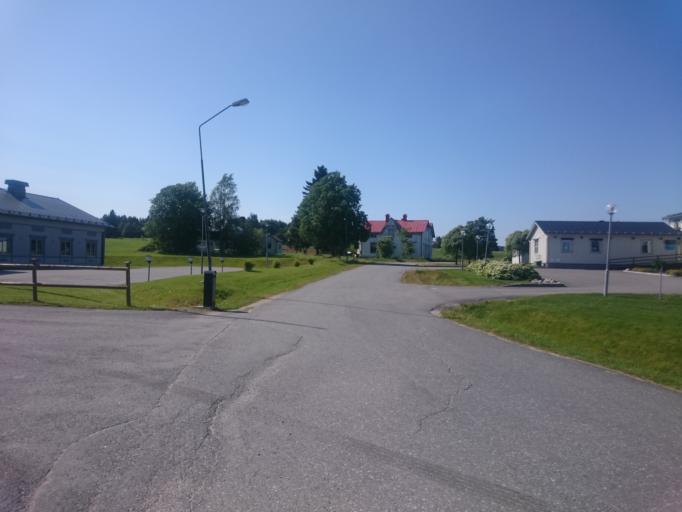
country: SE
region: Vaesternorrland
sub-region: OErnskoeldsviks Kommun
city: Bredbyn
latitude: 63.3005
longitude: 18.2801
